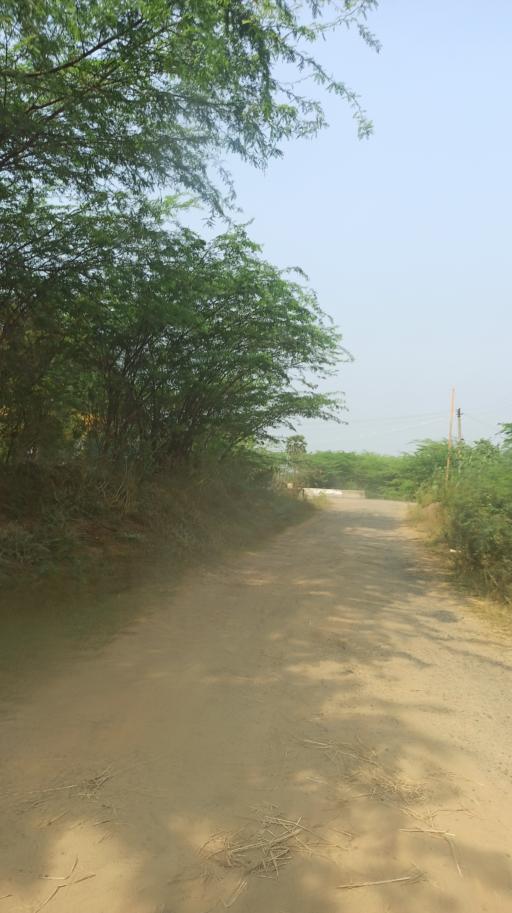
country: IN
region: Tamil Nadu
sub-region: Tiruvannamalai
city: Desur
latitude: 12.4365
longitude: 79.3910
